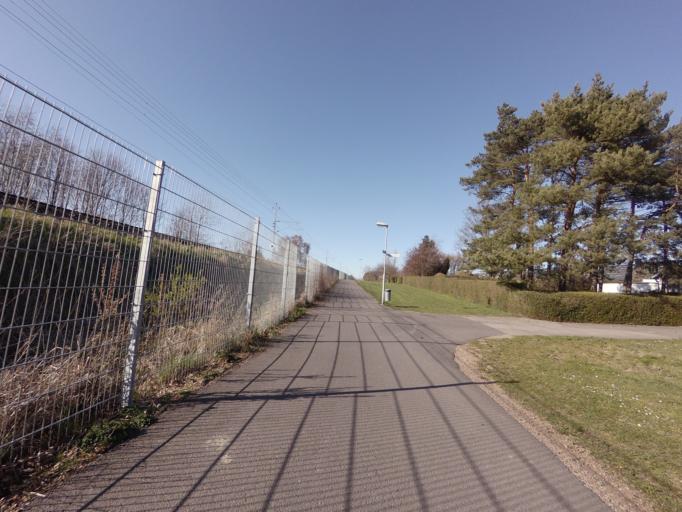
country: SE
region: Skane
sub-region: Lomma Kommun
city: Lomma
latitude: 55.6644
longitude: 13.0748
